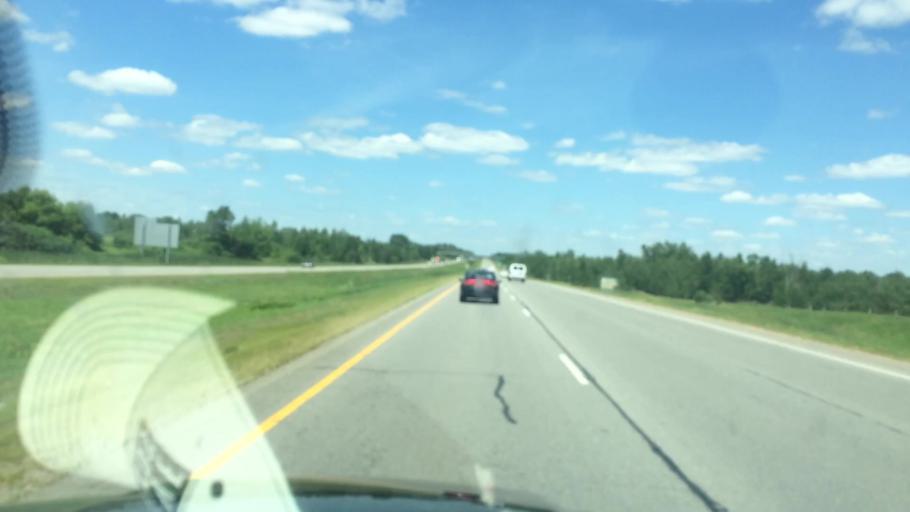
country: US
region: Wisconsin
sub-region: Marathon County
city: Mosinee
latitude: 44.7337
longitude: -89.6795
